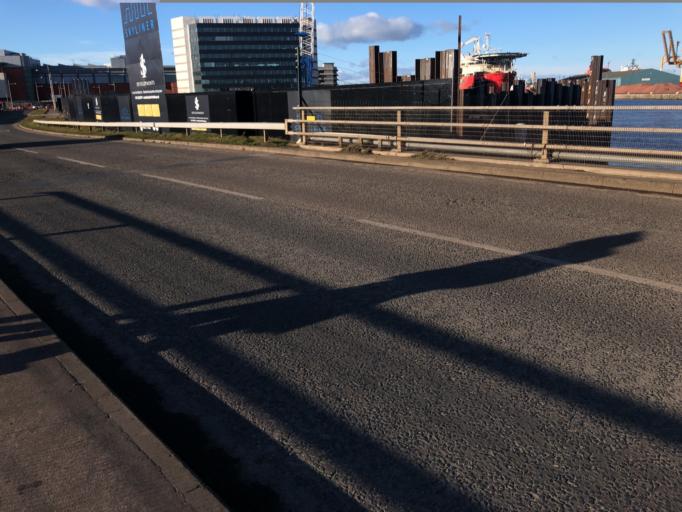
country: GB
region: Scotland
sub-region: West Lothian
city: Seafield
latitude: 55.9794
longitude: -3.1720
